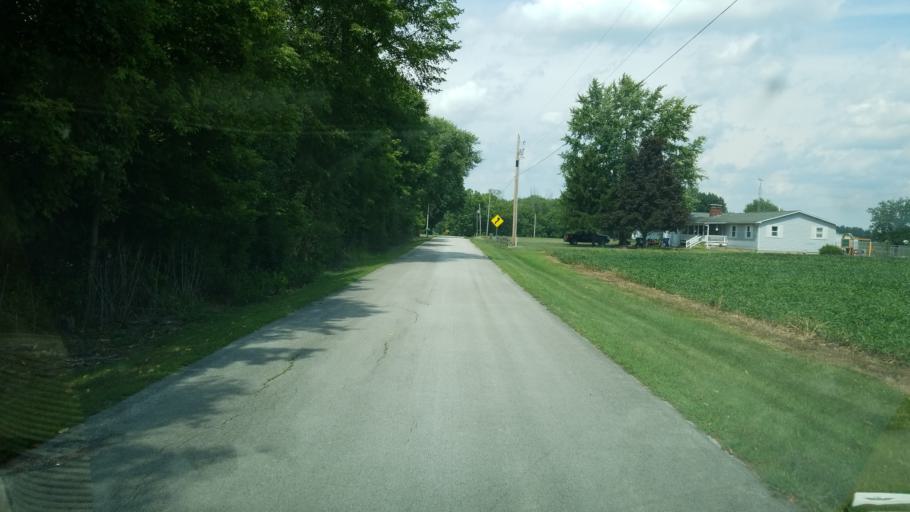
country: US
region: Ohio
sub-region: Hancock County
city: Arlington
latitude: 40.9230
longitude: -83.5470
